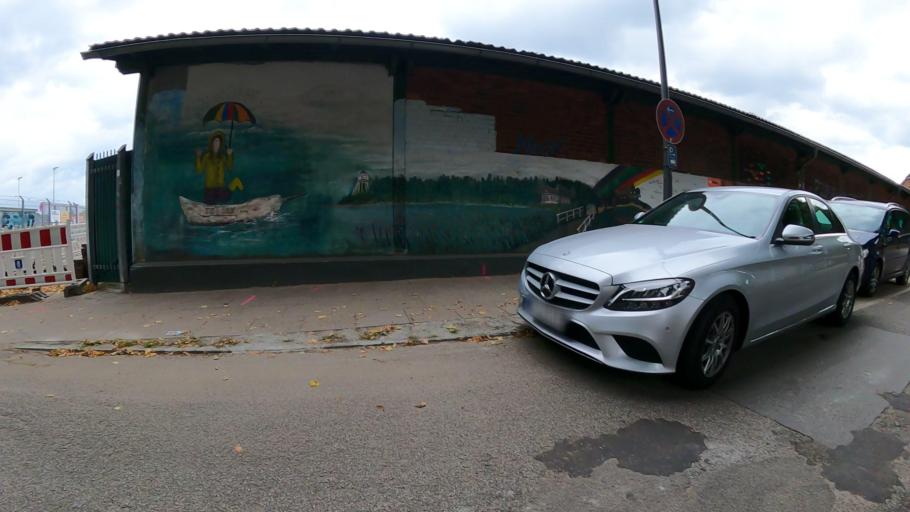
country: DE
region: Hamburg
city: Altona
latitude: 53.5371
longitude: 9.8750
